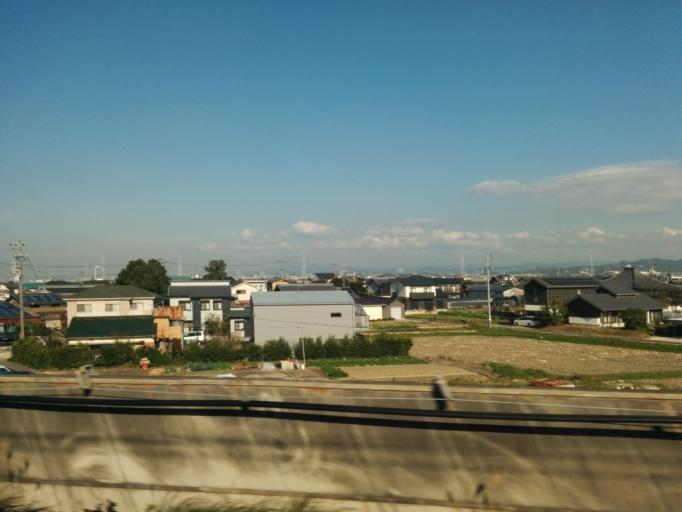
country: JP
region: Aichi
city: Okazaki
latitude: 34.8909
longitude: 137.1326
